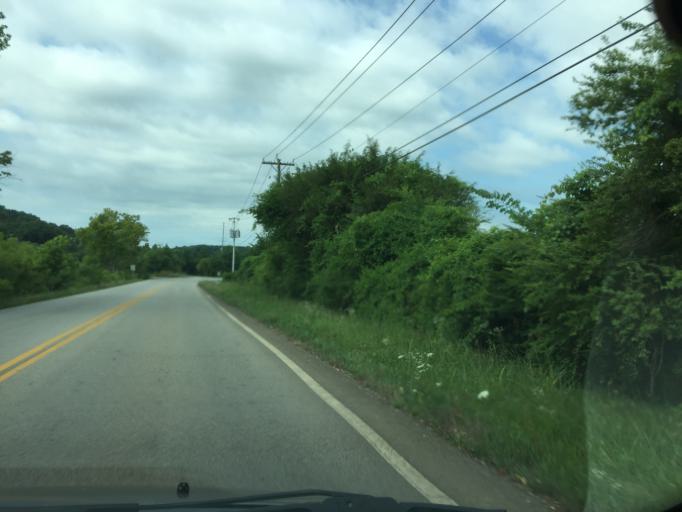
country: US
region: Tennessee
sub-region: Hamilton County
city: Apison
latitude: 34.9897
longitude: -85.0618
